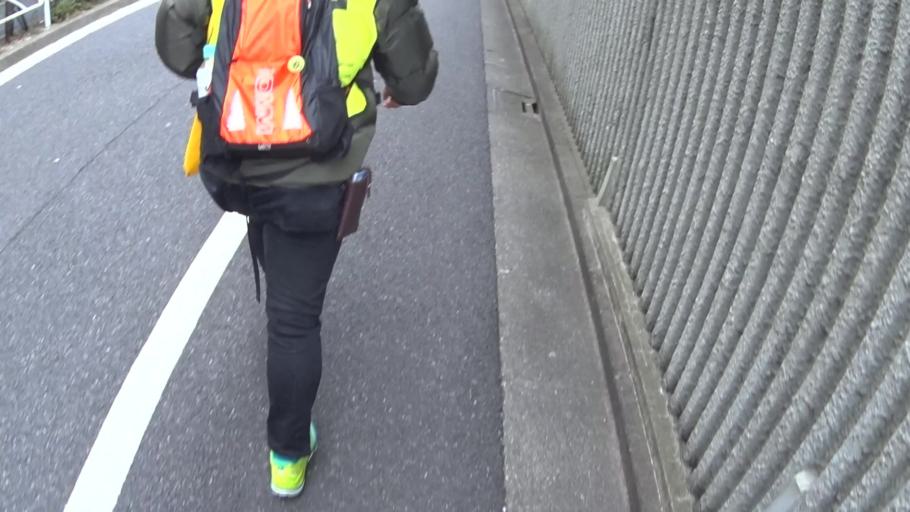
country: JP
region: Tokyo
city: Tokyo
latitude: 35.6540
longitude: 139.6903
